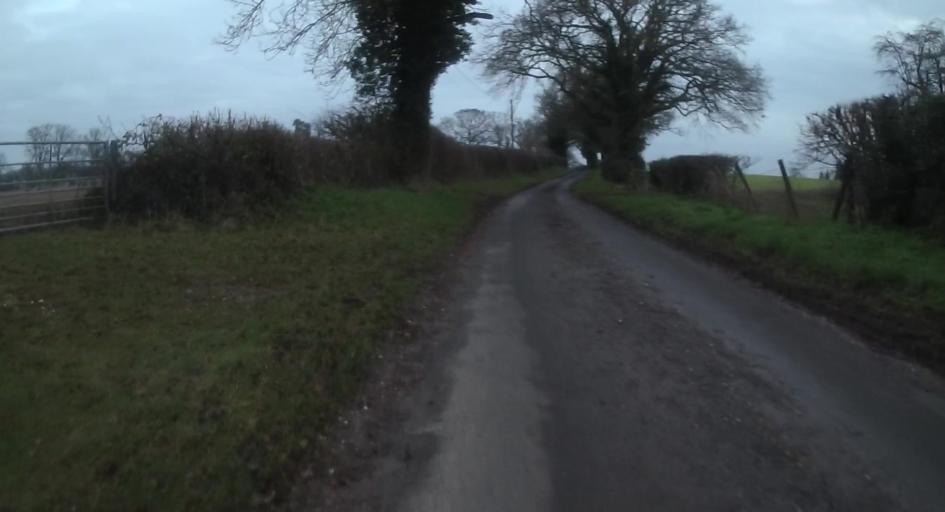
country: GB
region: England
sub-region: Hampshire
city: Overton
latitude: 51.2573
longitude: -1.3073
